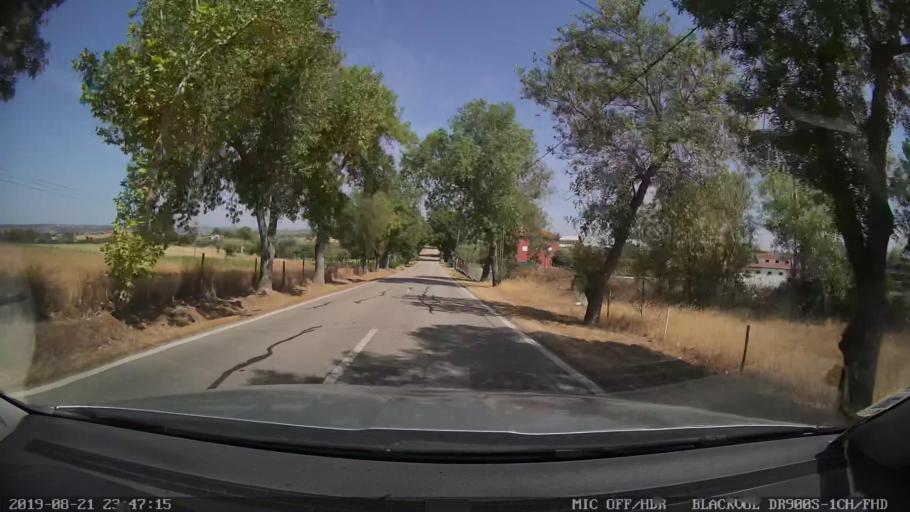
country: PT
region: Castelo Branco
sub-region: Idanha-A-Nova
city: Idanha-a-Nova
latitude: 39.8494
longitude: -7.2572
